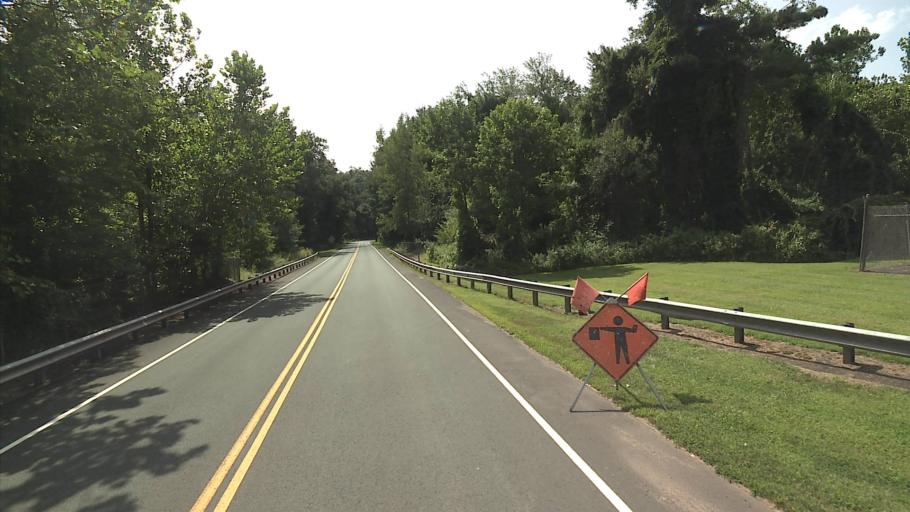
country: US
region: Connecticut
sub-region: Hartford County
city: Broad Brook
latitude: 41.9140
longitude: -72.5560
